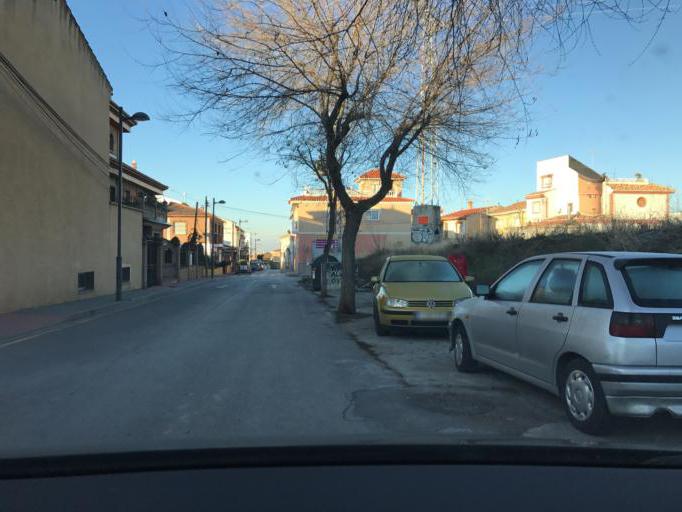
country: ES
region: Andalusia
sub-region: Provincia de Granada
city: Pulianas
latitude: 37.2194
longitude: -3.6026
